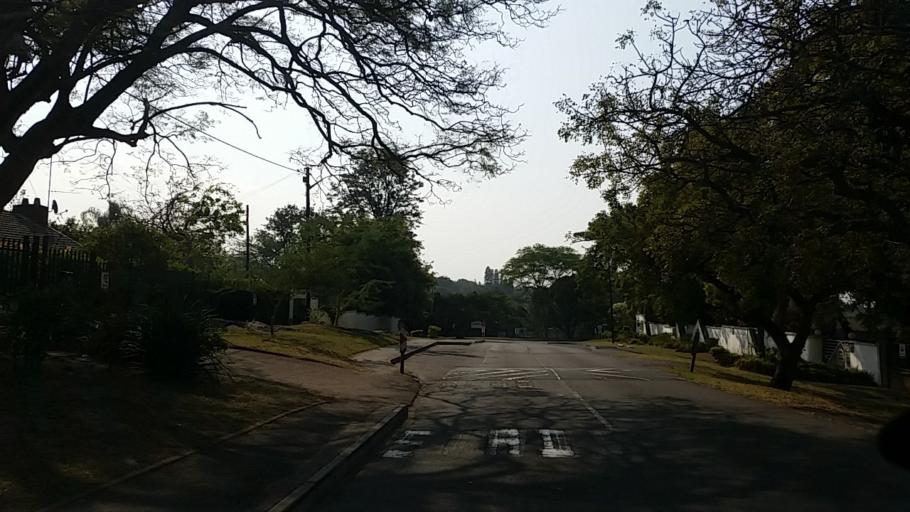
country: ZA
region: KwaZulu-Natal
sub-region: eThekwini Metropolitan Municipality
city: Berea
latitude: -29.8392
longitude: 30.9409
